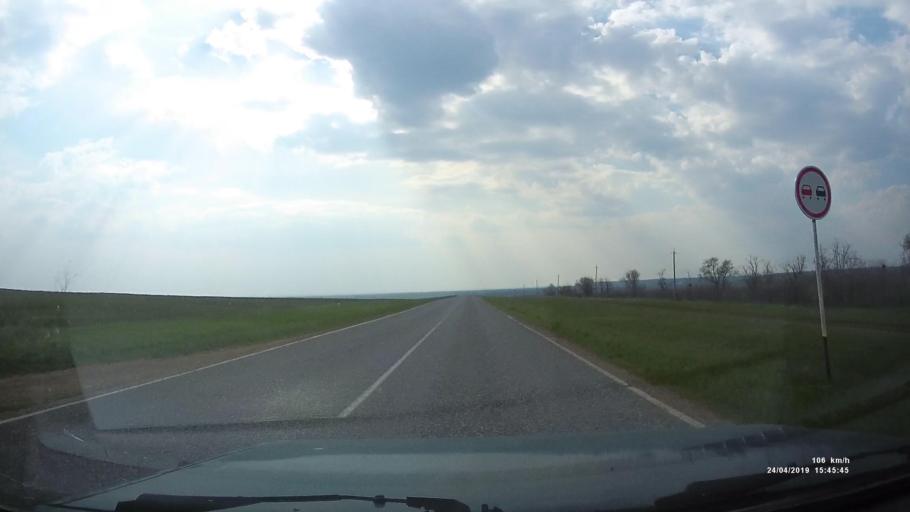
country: RU
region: Kalmykiya
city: Yashalta
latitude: 46.5918
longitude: 42.7303
